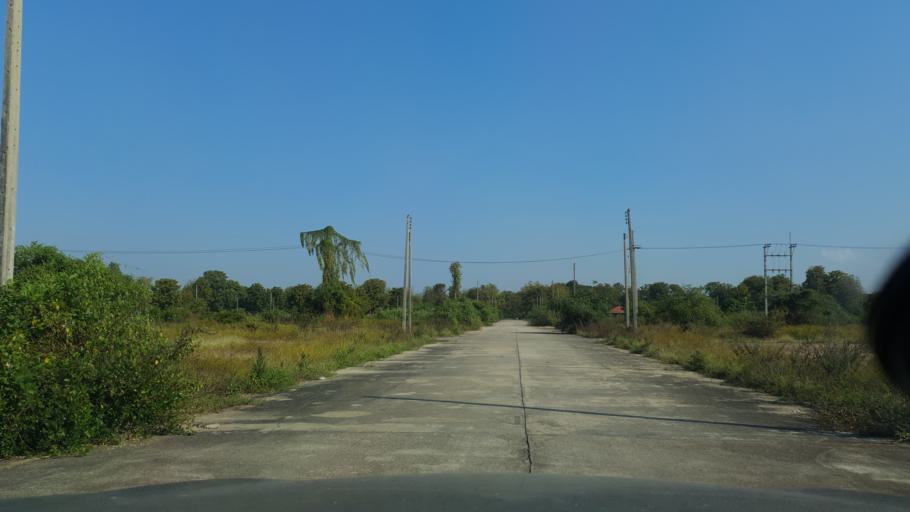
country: TH
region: Lamphun
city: Ban Thi
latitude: 18.6754
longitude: 99.1225
